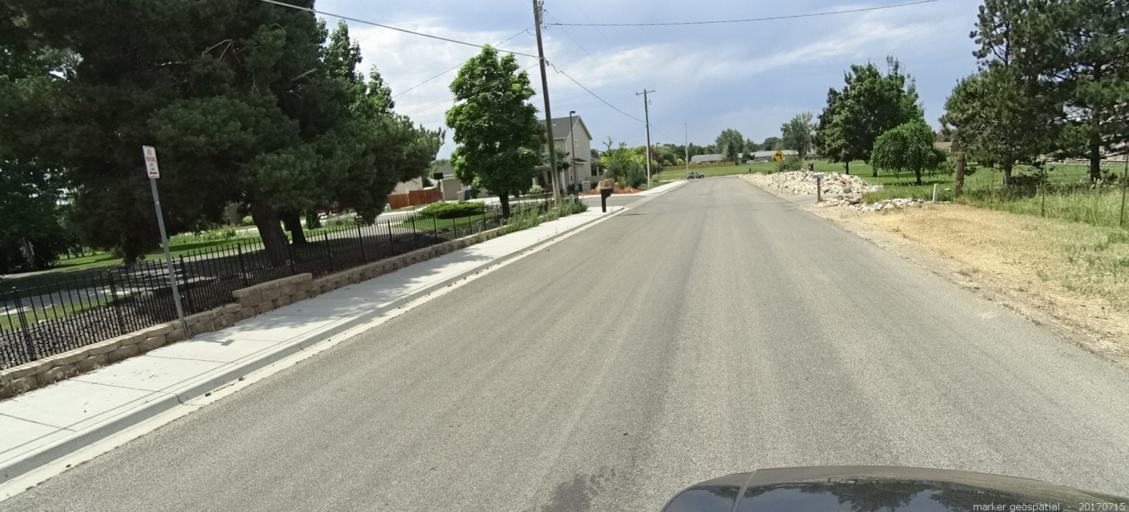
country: US
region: Idaho
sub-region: Ada County
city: Garden City
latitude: 43.5694
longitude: -116.3062
